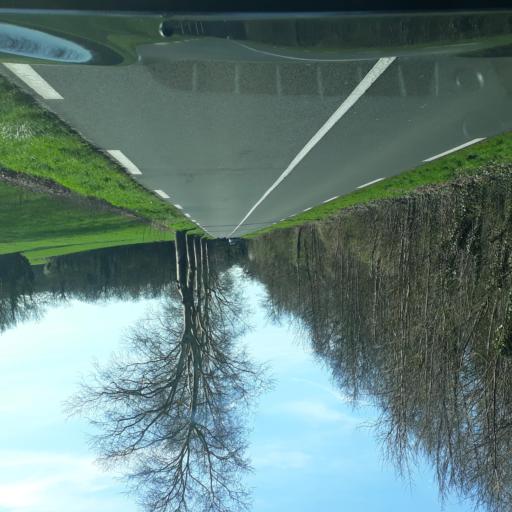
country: FR
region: Ile-de-France
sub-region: Departement de l'Essonne
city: Boissy-le-Cutte
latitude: 48.4585
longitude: 2.2628
